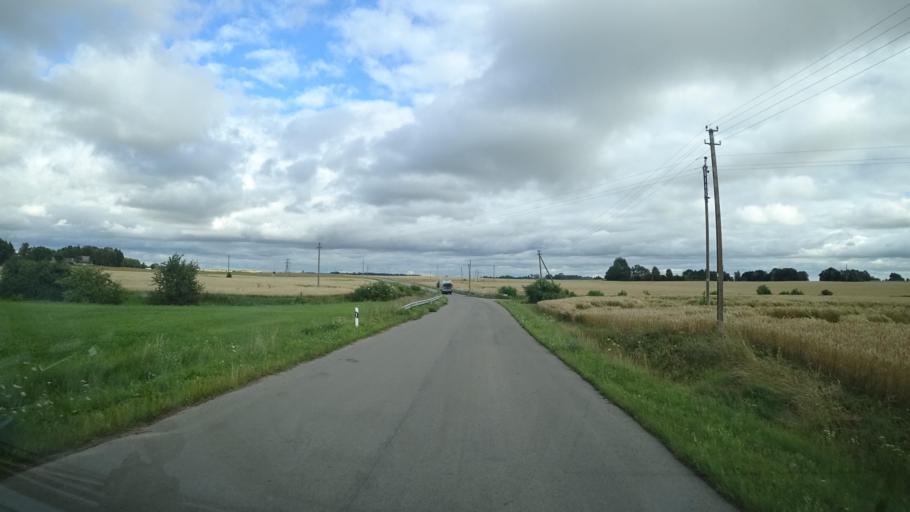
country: LT
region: Marijampoles apskritis
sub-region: Marijampole Municipality
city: Marijampole
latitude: 54.5189
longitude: 23.3227
